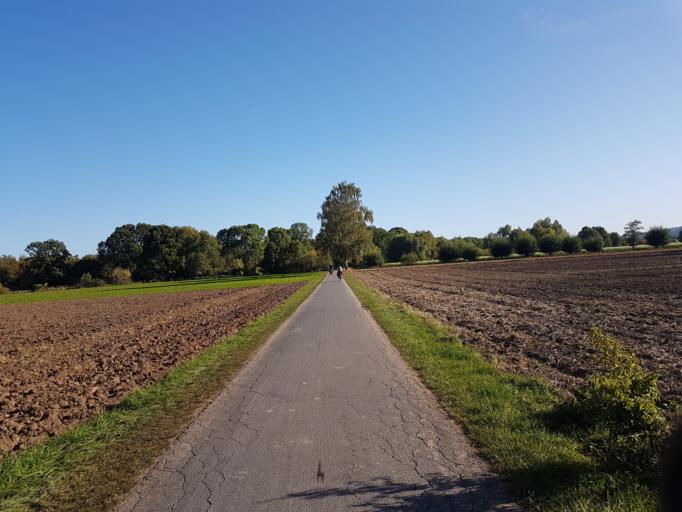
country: DE
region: North Rhine-Westphalia
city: Bad Oeynhausen
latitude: 52.2345
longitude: 8.8390
